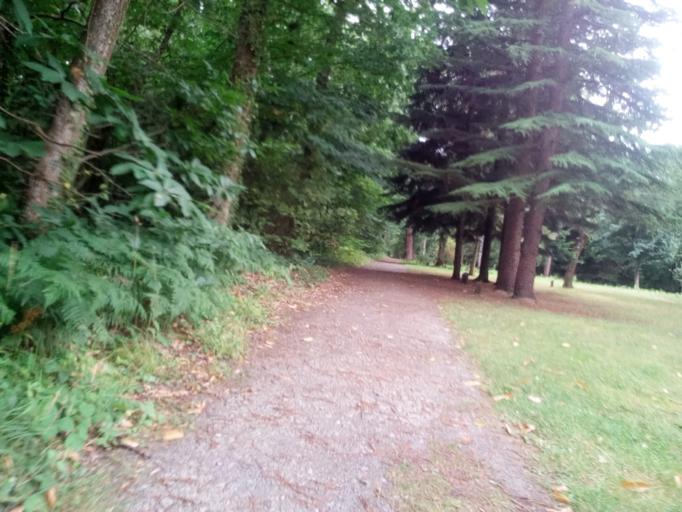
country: FR
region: Lower Normandy
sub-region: Departement du Calvados
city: Clinchamps-sur-Orne
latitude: 49.0427
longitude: -0.4265
